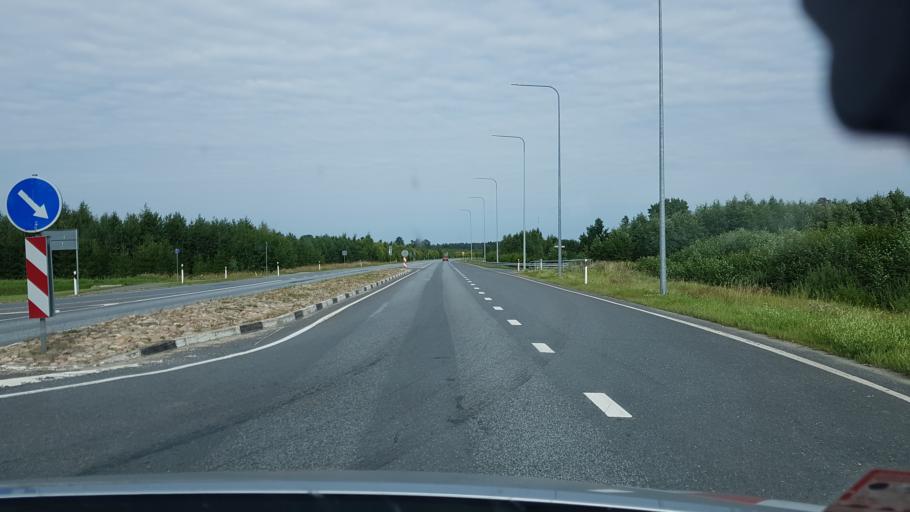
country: EE
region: Raplamaa
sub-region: Kohila vald
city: Kohila
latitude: 59.1705
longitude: 24.7724
